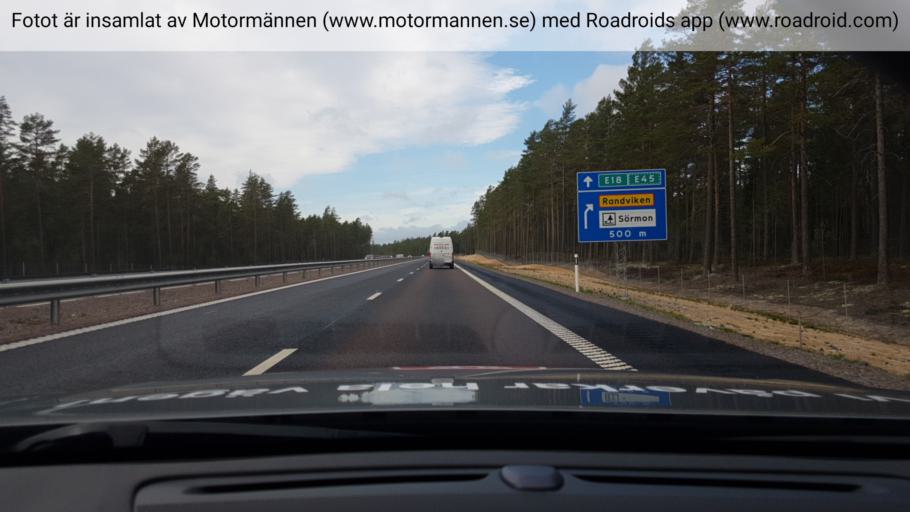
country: SE
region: Vaermland
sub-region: Hammaro Kommun
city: Skoghall
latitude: 59.3839
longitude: 13.3567
